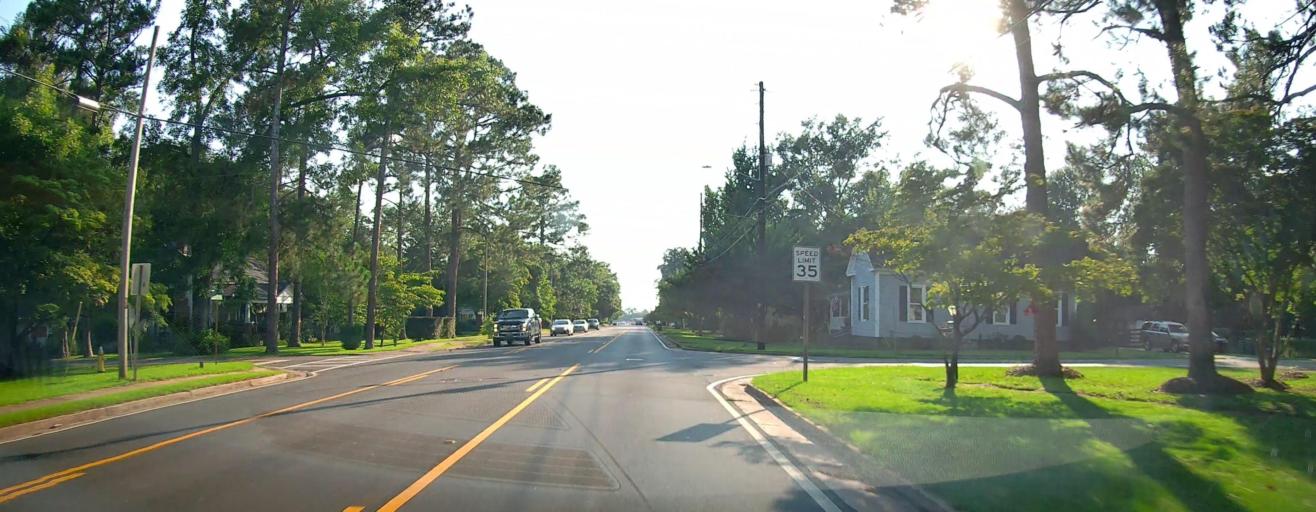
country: US
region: Georgia
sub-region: Houston County
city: Perry
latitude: 32.4623
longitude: -83.7249
